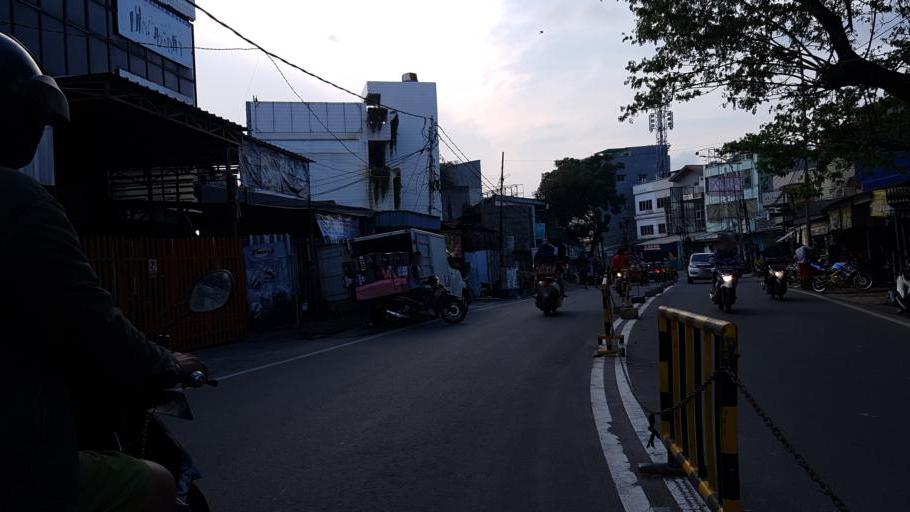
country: ID
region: Jakarta Raya
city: Jakarta
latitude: -6.1383
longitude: 106.7859
